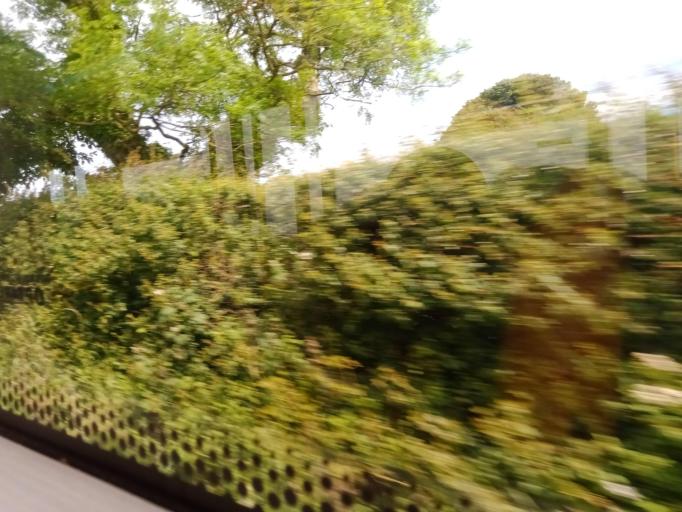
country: GB
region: Wales
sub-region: Anglesey
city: Beaumaris
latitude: 53.2741
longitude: -4.1178
